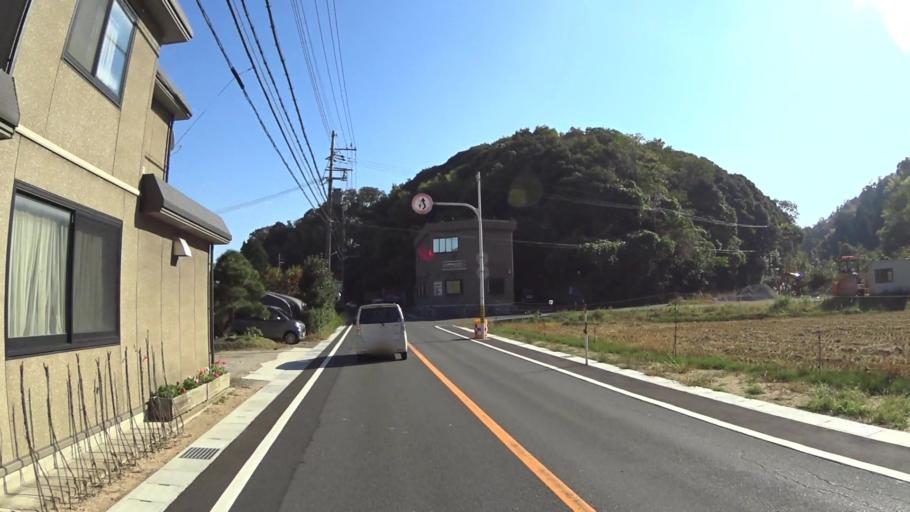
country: JP
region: Kyoto
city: Miyazu
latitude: 35.6654
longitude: 135.0284
